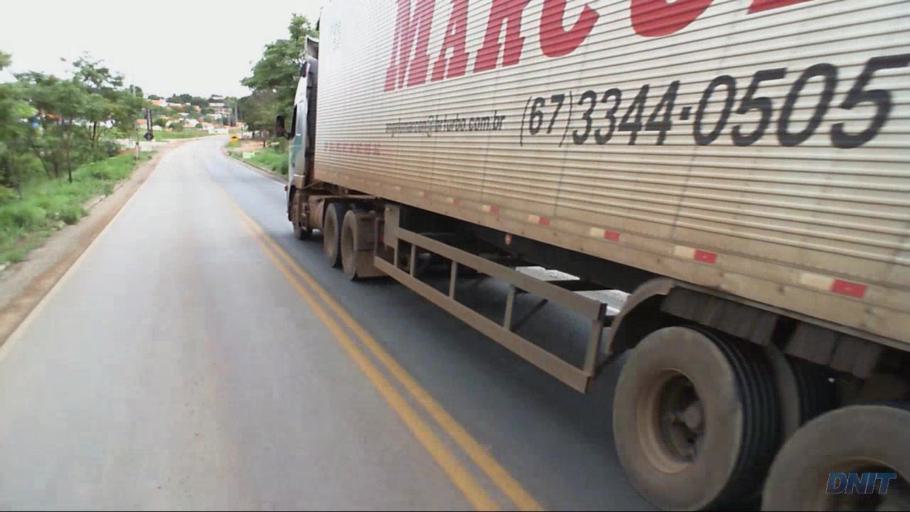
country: BR
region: Goias
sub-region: Padre Bernardo
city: Padre Bernardo
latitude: -15.1785
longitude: -48.2855
